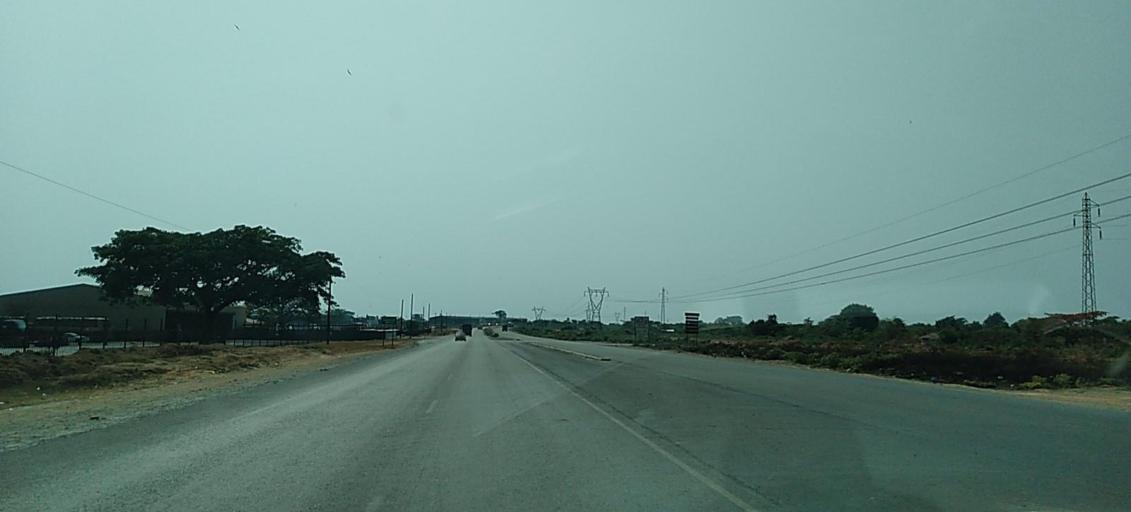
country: ZM
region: Copperbelt
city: Chingola
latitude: -12.5676
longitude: 27.9003
